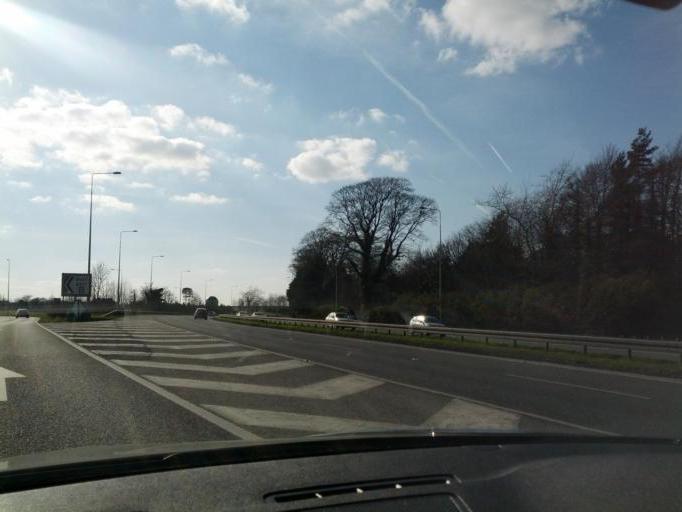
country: IE
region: Leinster
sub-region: Kildare
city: Johnstown
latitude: 53.2352
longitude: -6.6286
